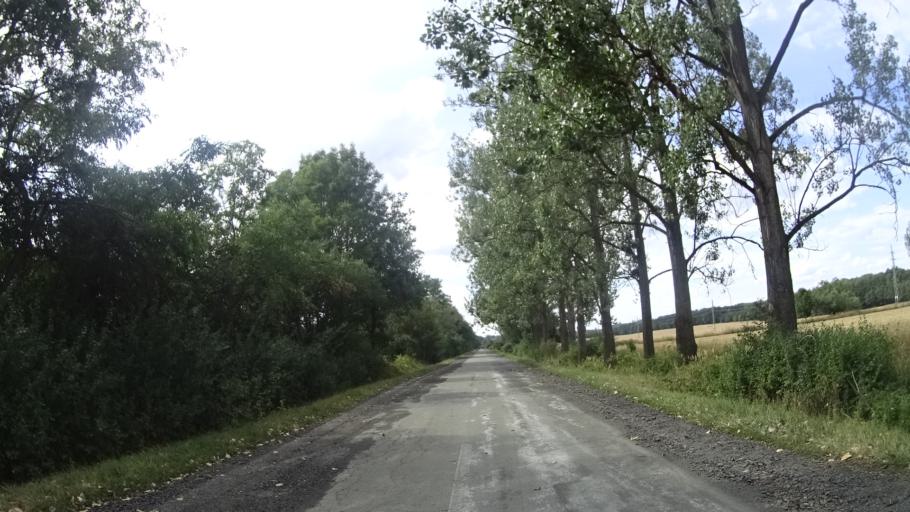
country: CZ
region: Olomoucky
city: Cervenka
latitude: 49.7159
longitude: 17.0486
